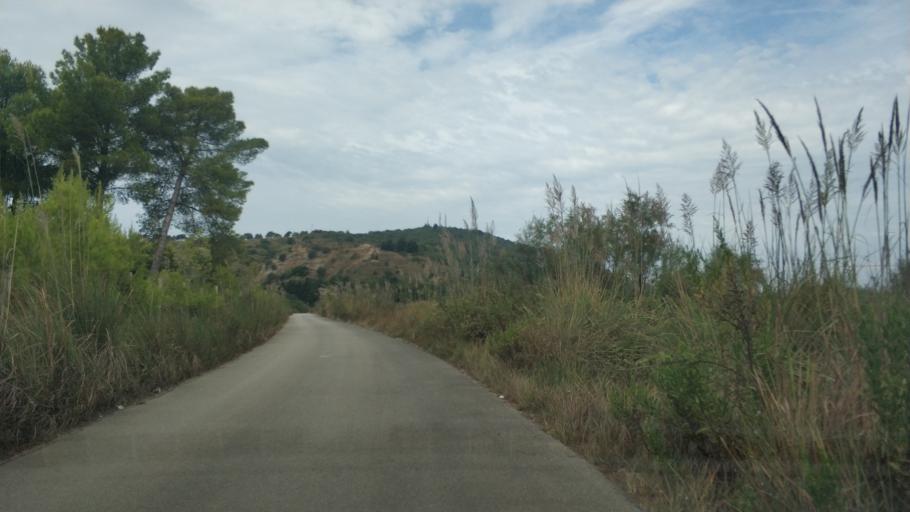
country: AL
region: Vlore
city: Vlore
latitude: 40.5044
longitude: 19.4251
